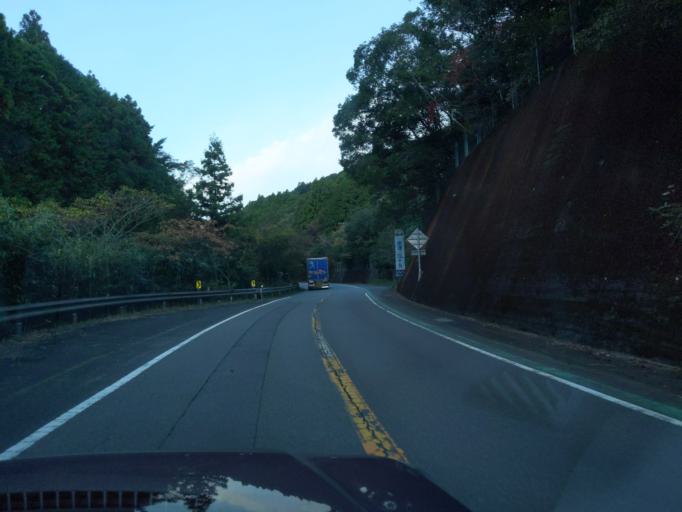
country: JP
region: Tokushima
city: Anan
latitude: 33.7075
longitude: 134.4620
